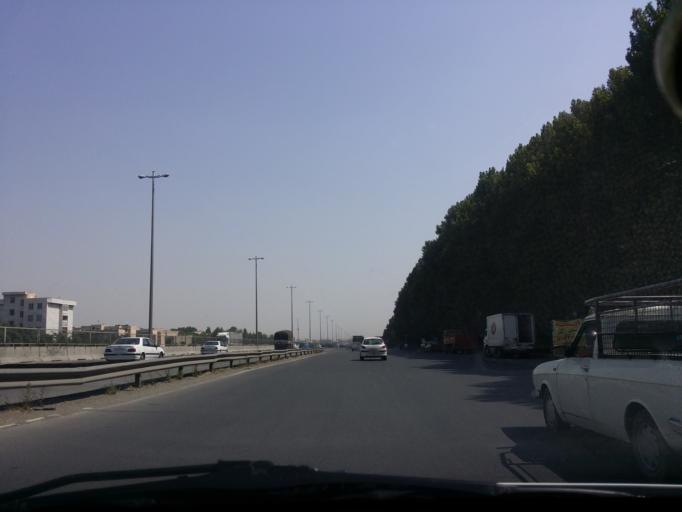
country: IR
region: Alborz
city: Karaj
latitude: 35.8471
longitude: 50.9090
